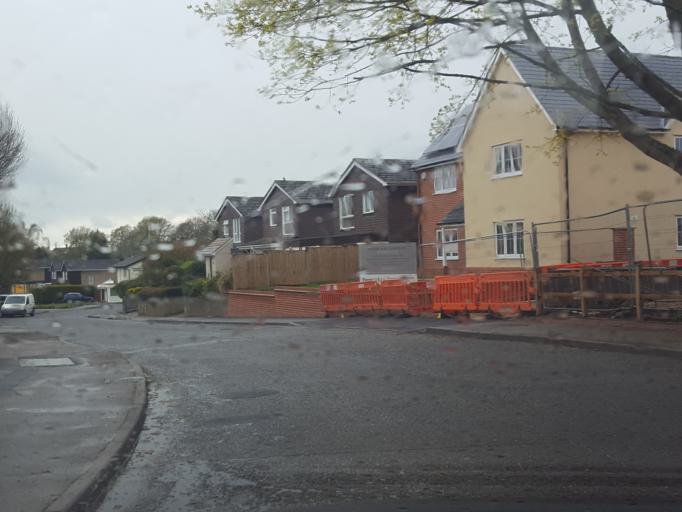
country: GB
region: England
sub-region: Essex
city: Great Horkesley
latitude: 51.9246
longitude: 0.8804
